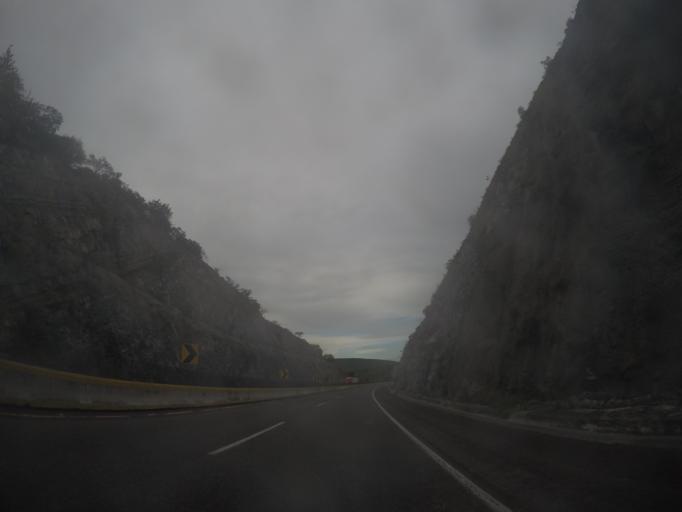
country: MX
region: Guerrero
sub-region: Eduardo Neri
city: Tlanipatla
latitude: 17.8384
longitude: -99.4483
